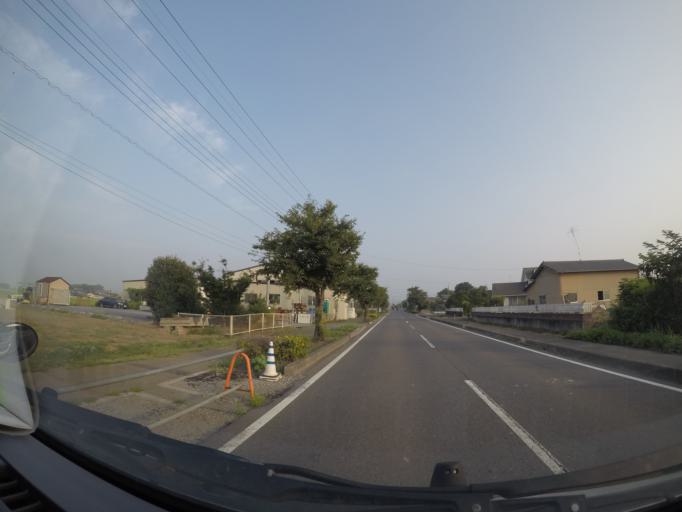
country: JP
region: Tochigi
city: Fujioka
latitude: 36.2678
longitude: 139.7170
